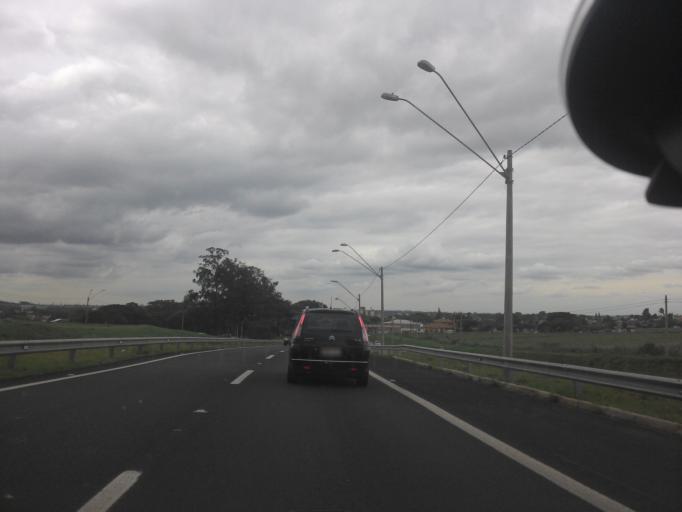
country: BR
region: Sao Paulo
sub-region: Campinas
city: Campinas
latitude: -22.8386
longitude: -47.0797
